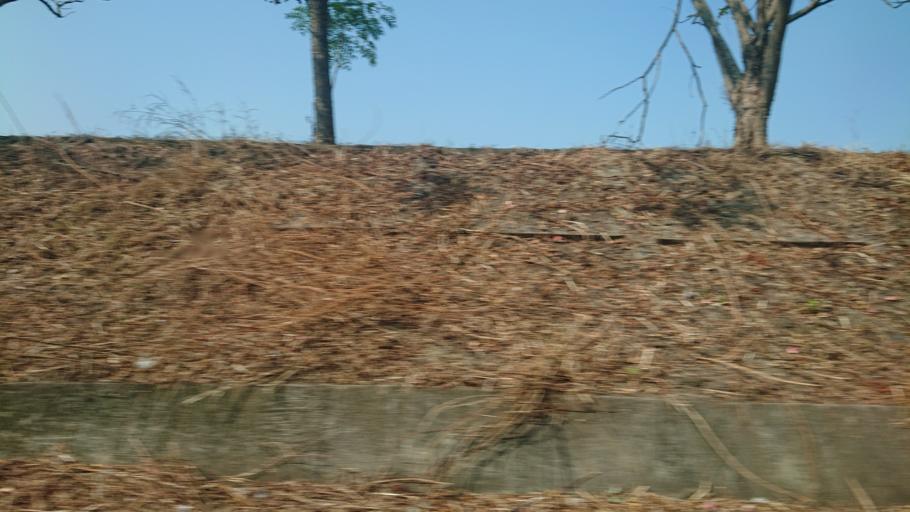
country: TW
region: Taiwan
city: Lugu
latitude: 23.7474
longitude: 120.6587
